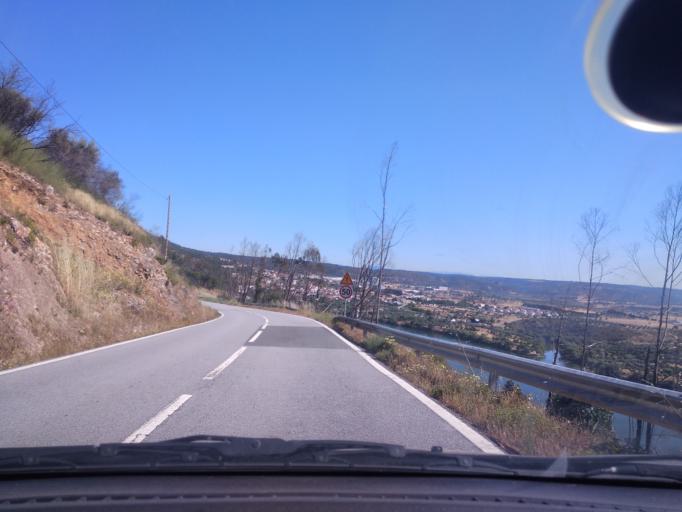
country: PT
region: Portalegre
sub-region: Nisa
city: Nisa
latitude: 39.6379
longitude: -7.6674
